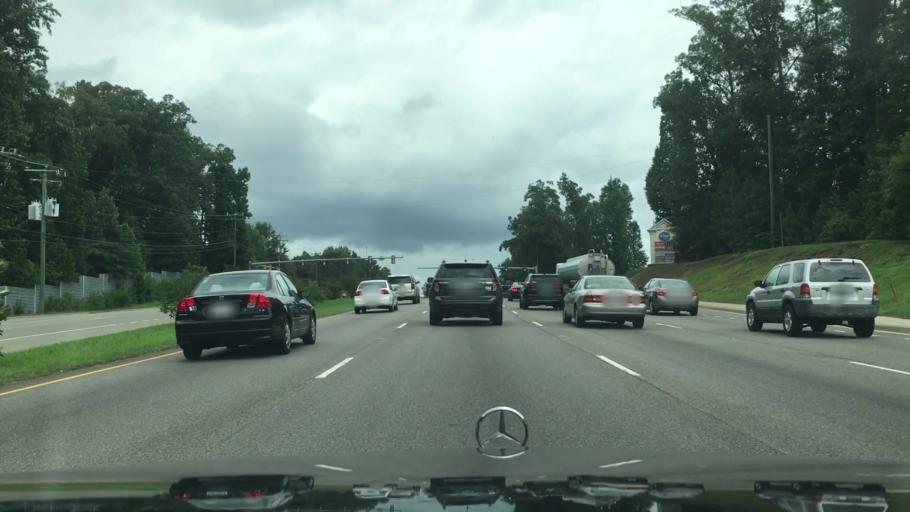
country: US
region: Virginia
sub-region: Chesterfield County
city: Brandermill
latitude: 37.4166
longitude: -77.6413
